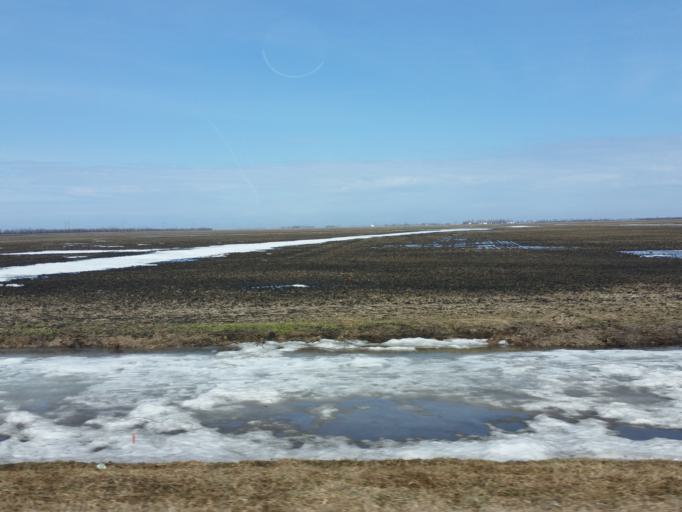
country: US
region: North Dakota
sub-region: Walsh County
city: Grafton
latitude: 48.2954
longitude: -97.2600
